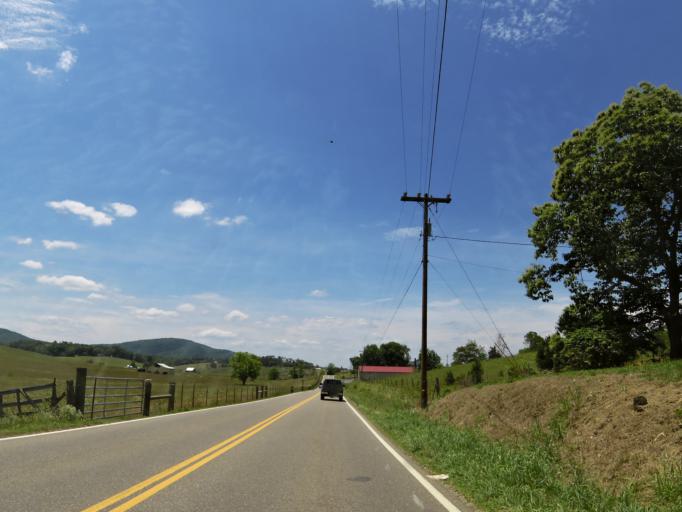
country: US
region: Tennessee
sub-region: Jefferson County
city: Dandridge
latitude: 35.9130
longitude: -83.3663
